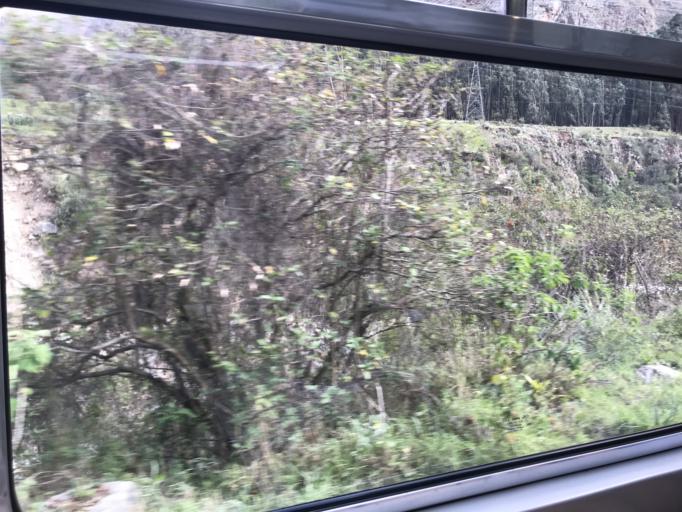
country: PE
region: Cusco
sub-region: Provincia de Urubamba
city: Ollantaytambo
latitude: -13.2250
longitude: -72.4283
